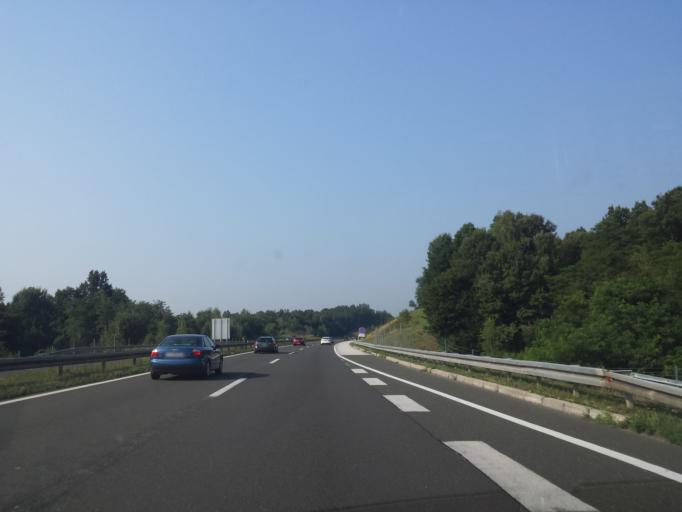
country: HR
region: Karlovacka
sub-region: Grad Karlovac
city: Karlovac
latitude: 45.4518
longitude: 15.3733
